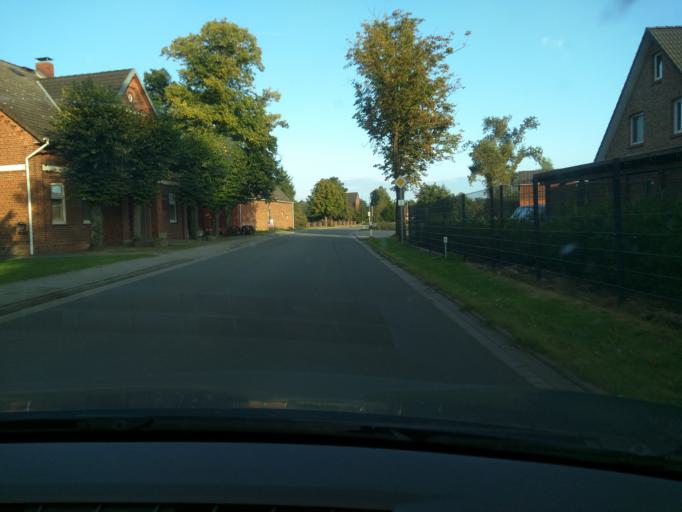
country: DE
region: Lower Saxony
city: Tespe
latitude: 53.3882
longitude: 10.4462
